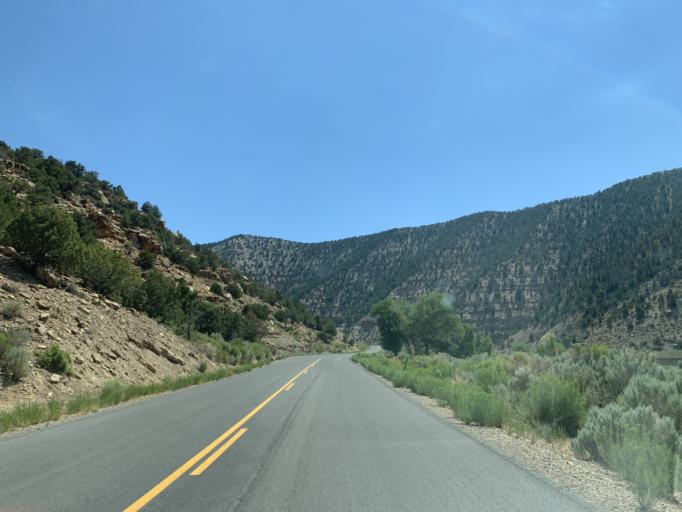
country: US
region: Utah
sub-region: Carbon County
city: East Carbon City
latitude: 39.7856
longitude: -110.4049
